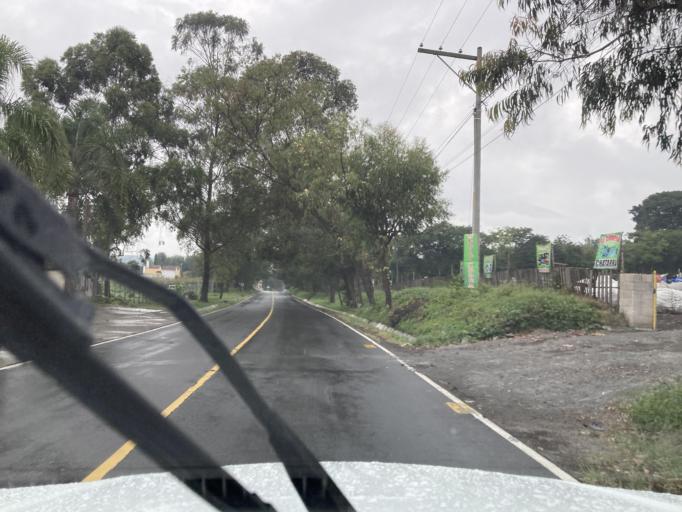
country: GT
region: Sacatepequez
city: San Miguel Duenas
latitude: 14.5196
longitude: -90.7798
